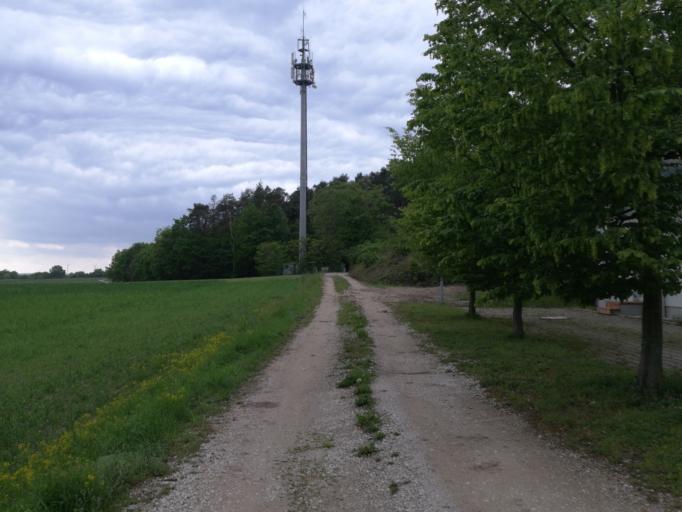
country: DE
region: Bavaria
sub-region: Regierungsbezirk Mittelfranken
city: Cadolzburg
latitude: 49.4547
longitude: 10.8704
